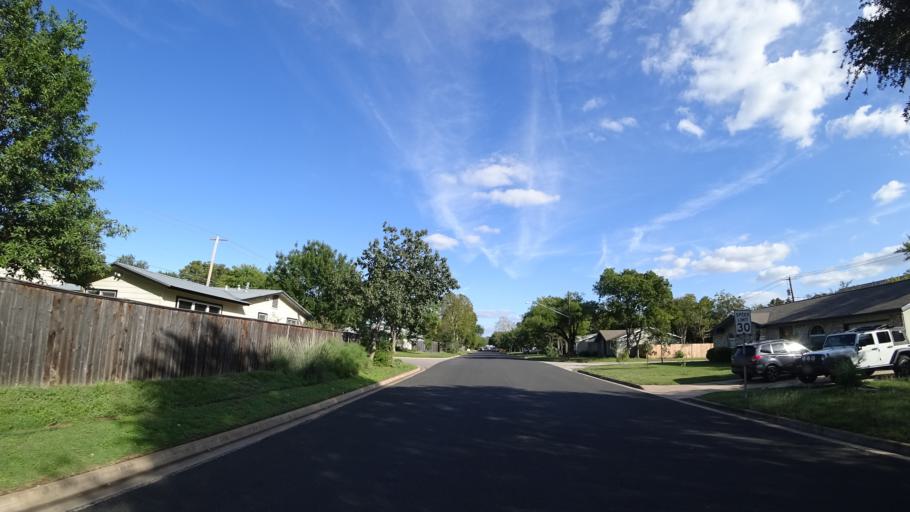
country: US
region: Texas
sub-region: Williamson County
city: Jollyville
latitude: 30.3612
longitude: -97.7355
